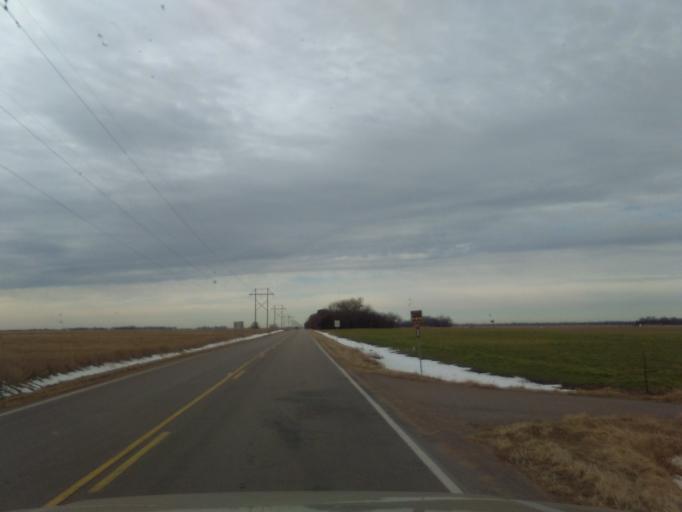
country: US
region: Nebraska
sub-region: Buffalo County
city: Gibbon
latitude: 40.6550
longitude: -98.8009
